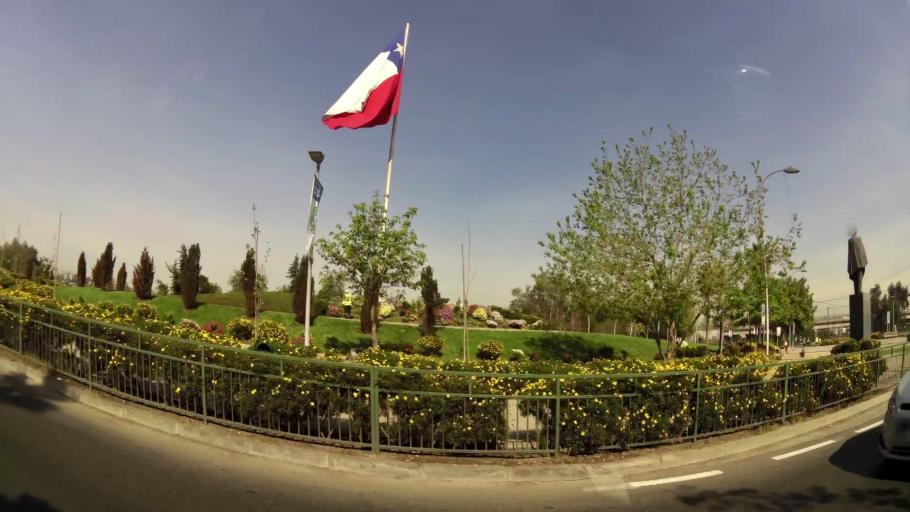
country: CL
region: Santiago Metropolitan
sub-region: Provincia de Santiago
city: Villa Presidente Frei, Nunoa, Santiago, Chile
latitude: -33.5109
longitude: -70.5879
